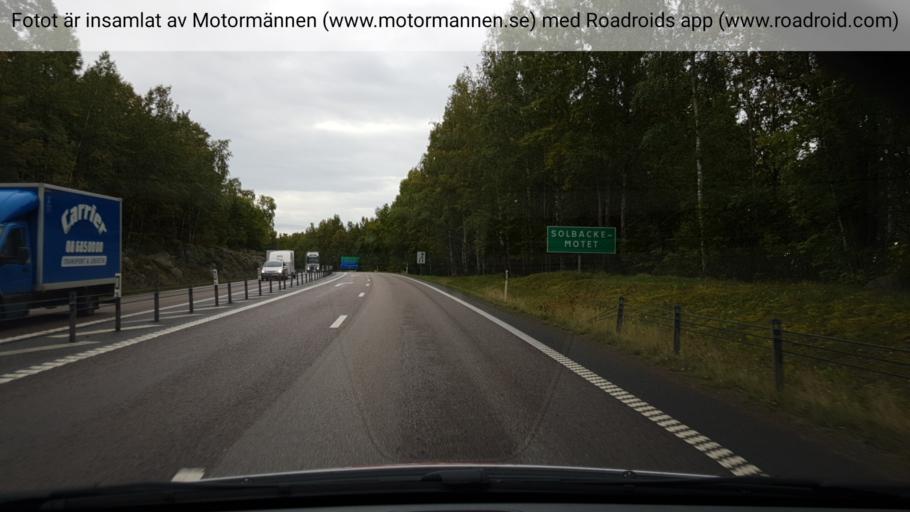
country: SE
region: Vaermland
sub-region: Kristinehamns Kommun
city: Kristinehamn
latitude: 59.3271
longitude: 14.1035
